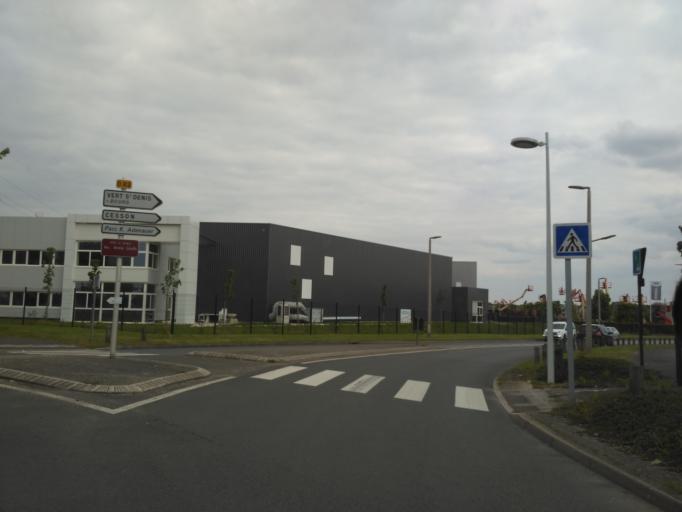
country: FR
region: Ile-de-France
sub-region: Departement de Seine-et-Marne
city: Vert-Saint-Denis
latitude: 48.5717
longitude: 2.6341
